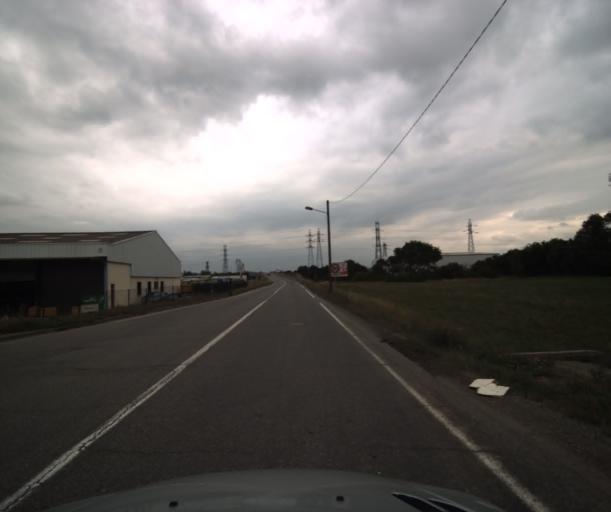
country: FR
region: Midi-Pyrenees
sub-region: Departement de la Haute-Garonne
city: Pinsaguel
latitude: 43.5264
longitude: 1.3778
